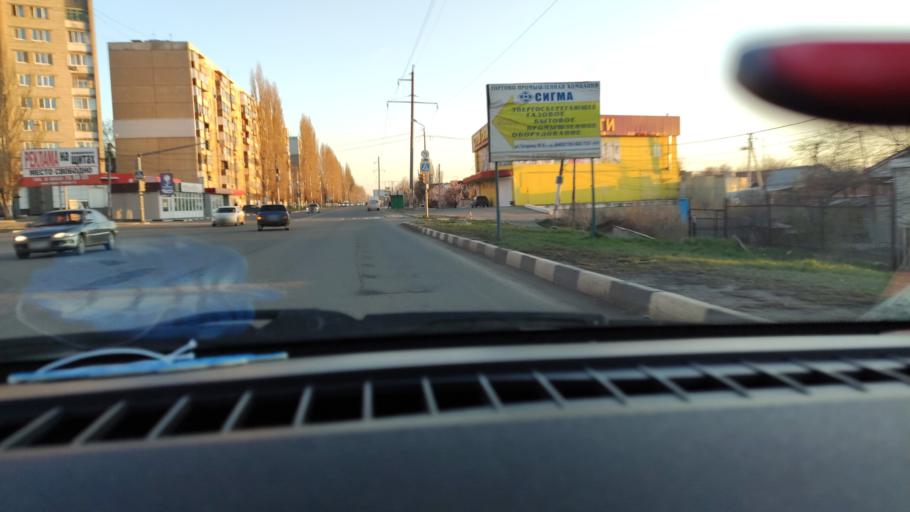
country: RU
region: Saratov
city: Privolzhskiy
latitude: 51.4098
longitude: 46.0413
